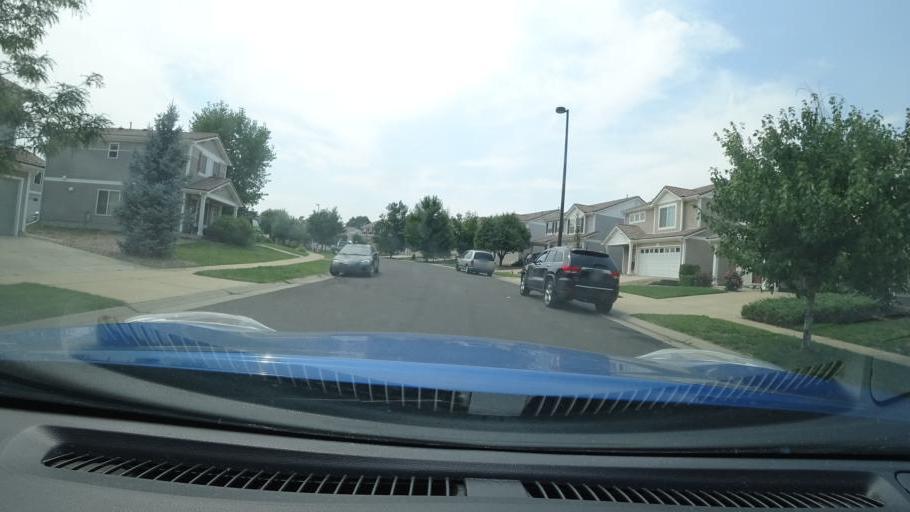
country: US
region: Colorado
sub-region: Adams County
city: Aurora
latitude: 39.7764
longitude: -104.7381
